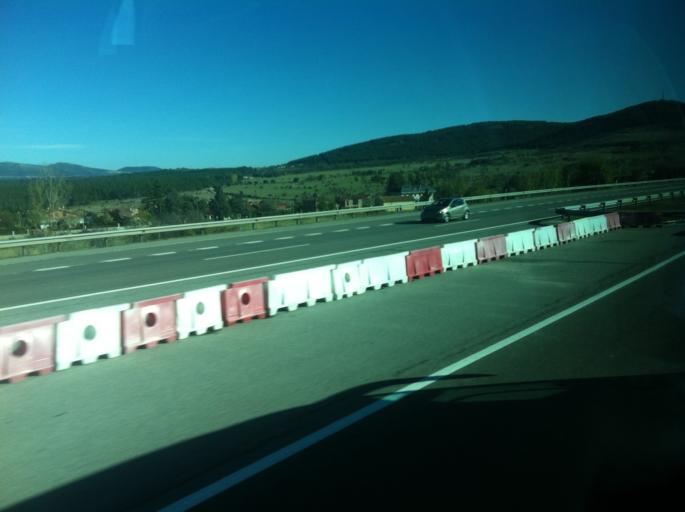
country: ES
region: Madrid
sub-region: Provincia de Madrid
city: Buitrago del Lozoya
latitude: 40.9846
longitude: -3.6402
